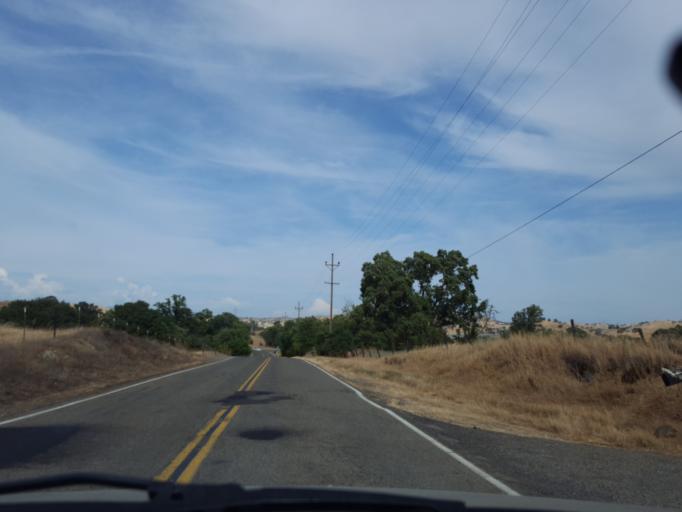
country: US
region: California
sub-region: Merced County
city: Planada
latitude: 37.5253
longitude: -120.3255
